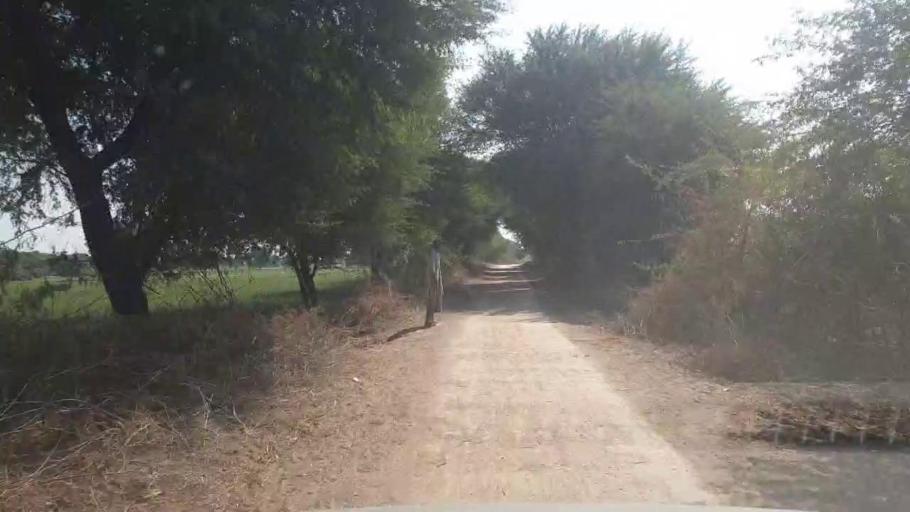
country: PK
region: Sindh
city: Chambar
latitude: 25.2734
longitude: 68.8138
